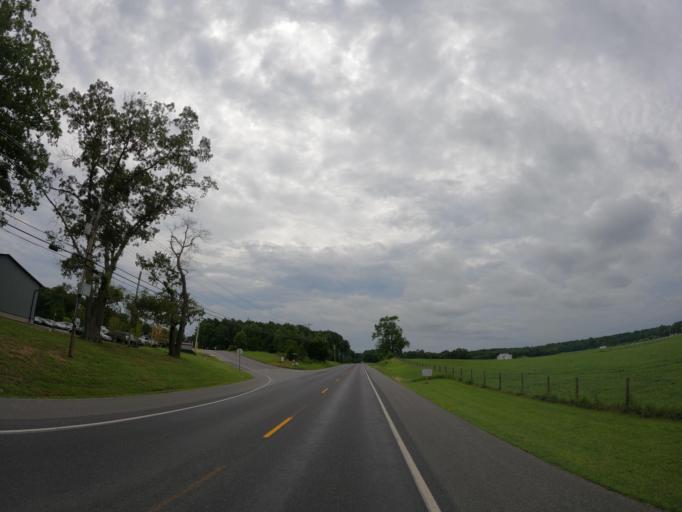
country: US
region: Maryland
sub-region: Saint Mary's County
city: Lexington Park
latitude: 38.2098
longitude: -76.5127
